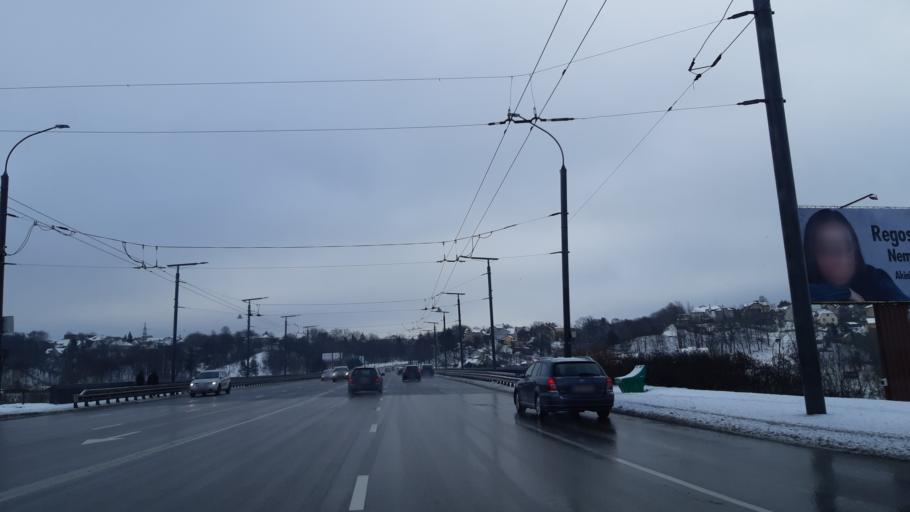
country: LT
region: Kauno apskritis
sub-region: Kaunas
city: Kaunas
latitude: 54.9144
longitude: 23.9062
